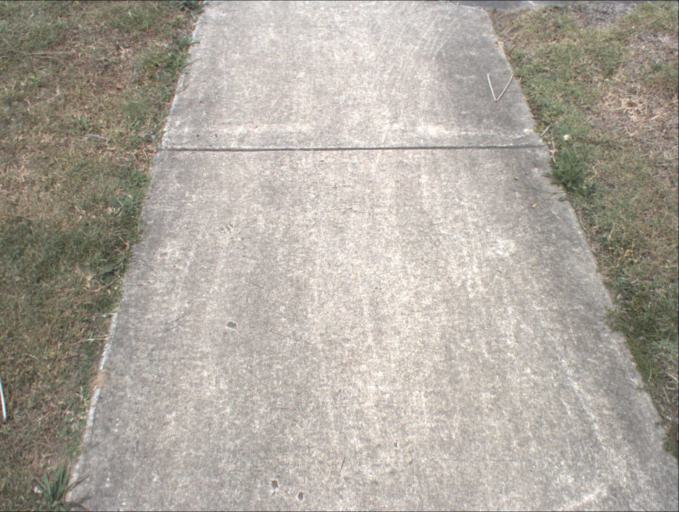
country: AU
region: Queensland
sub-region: Logan
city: Rochedale South
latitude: -27.5942
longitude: 153.1413
